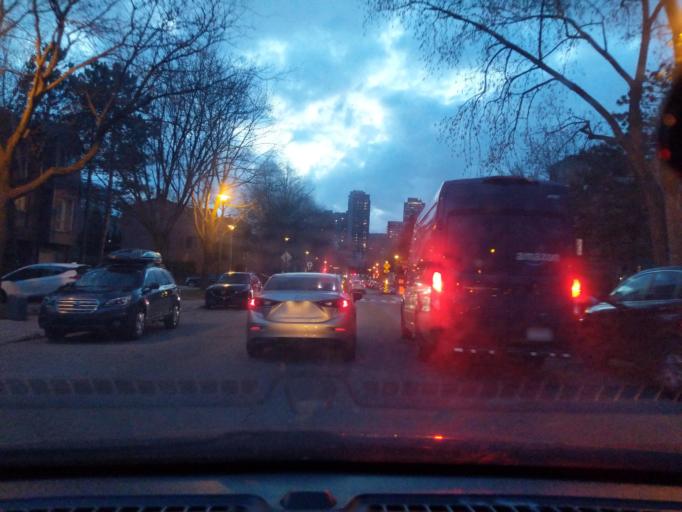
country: CA
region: Quebec
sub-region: Montreal
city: Montreal
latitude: 45.4884
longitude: -73.5705
